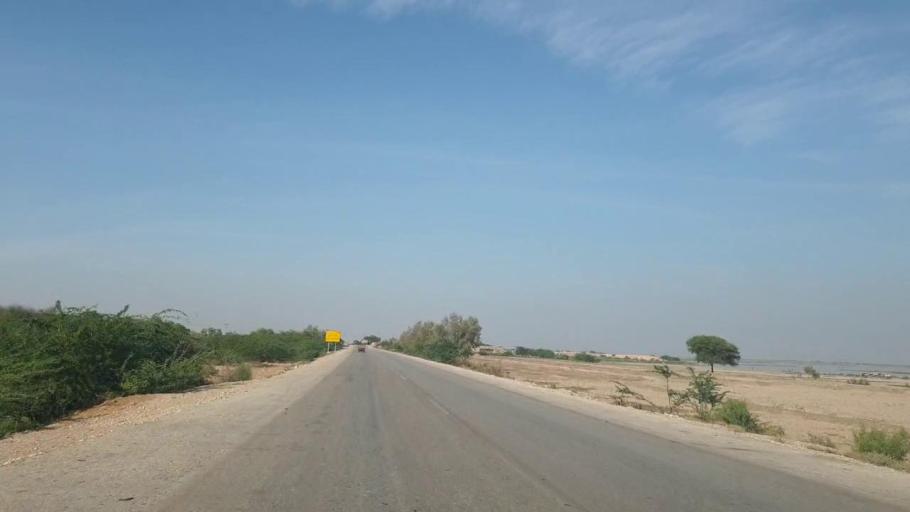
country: PK
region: Sindh
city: Sehwan
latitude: 26.3818
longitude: 67.8718
